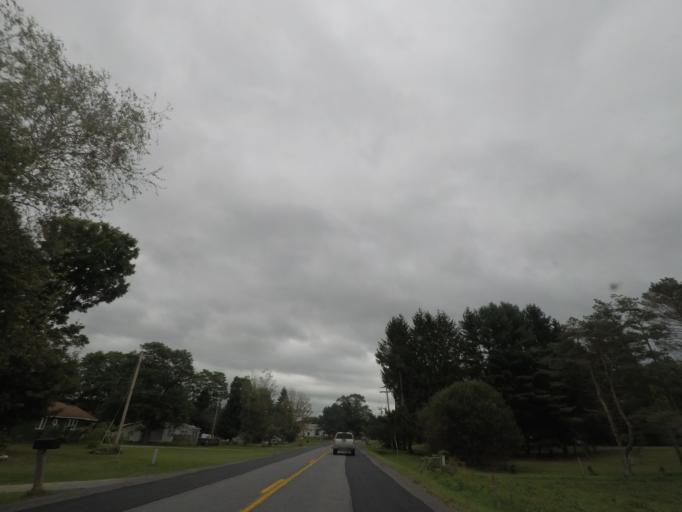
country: US
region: New York
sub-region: Rensselaer County
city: Hoosick Falls
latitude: 42.9515
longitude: -73.4090
